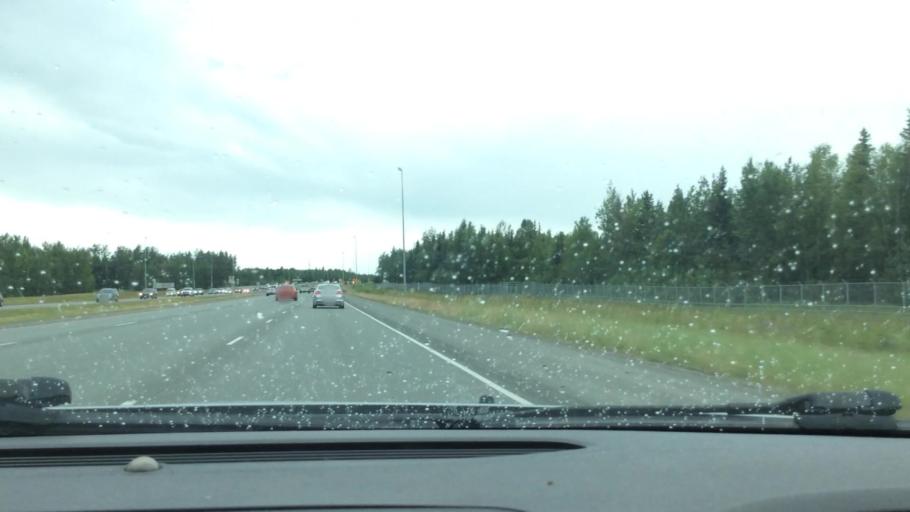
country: US
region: Alaska
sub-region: Anchorage Municipality
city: Elmendorf Air Force Base
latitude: 61.2428
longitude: -149.6851
